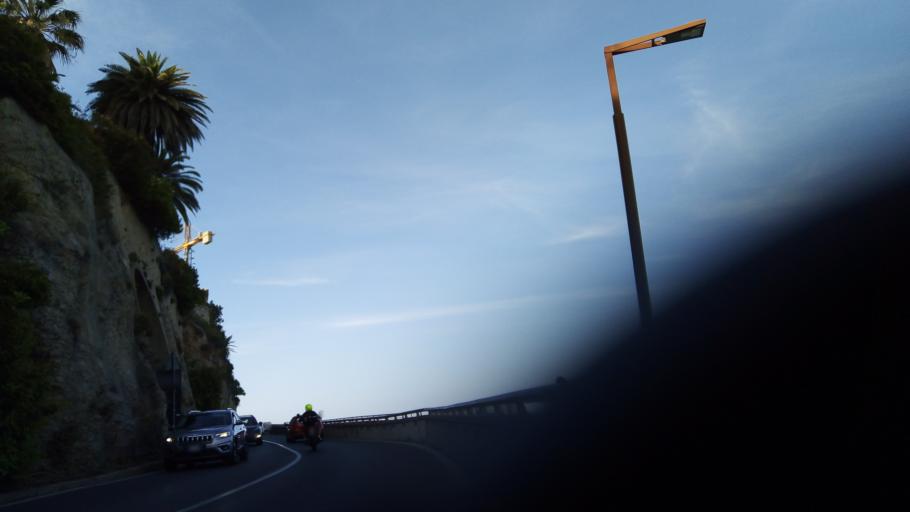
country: IT
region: Liguria
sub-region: Provincia di Savona
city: Borghetto Santo Spirito
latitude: 44.1027
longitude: 8.2376
